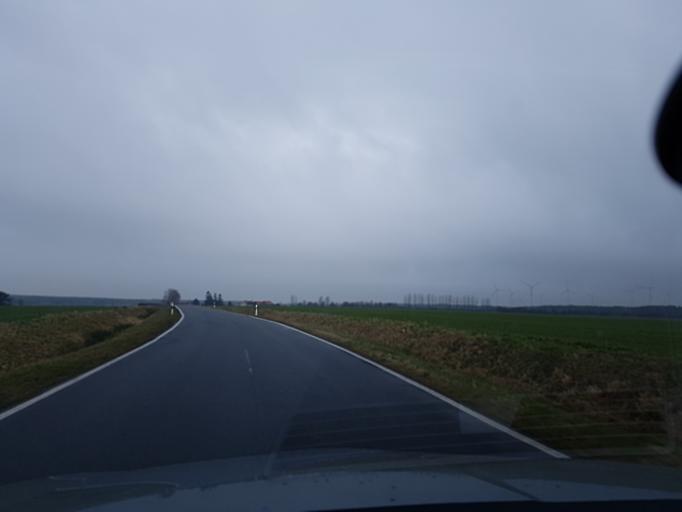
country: DE
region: Brandenburg
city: Trobitz
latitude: 51.6576
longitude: 13.4182
